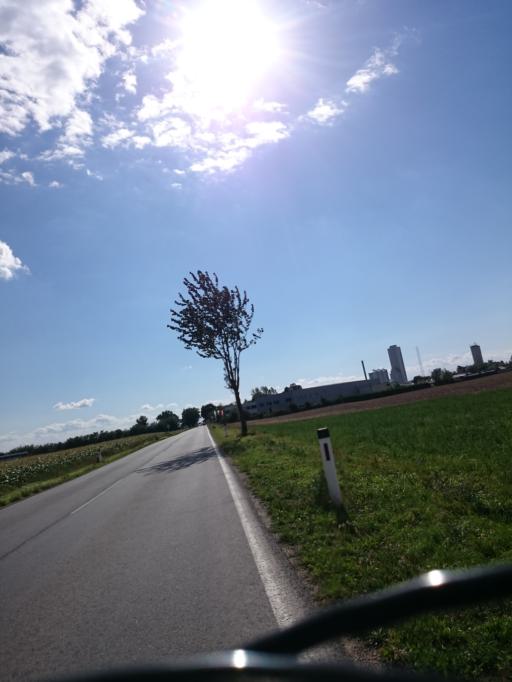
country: AT
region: Lower Austria
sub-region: Politischer Bezirk Ganserndorf
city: Raasdorf
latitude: 48.2424
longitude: 16.5943
